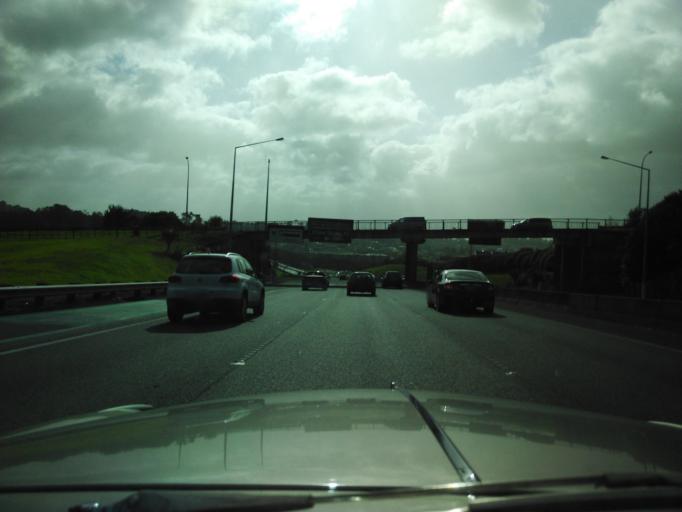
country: NZ
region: Auckland
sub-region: Auckland
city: Rothesay Bay
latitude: -36.7249
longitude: 174.7146
